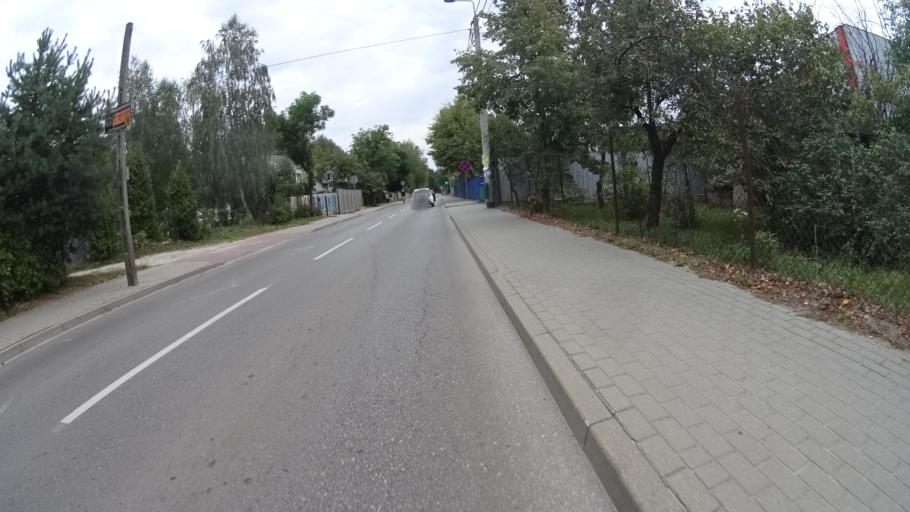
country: PL
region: Masovian Voivodeship
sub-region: Powiat pruszkowski
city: Granica
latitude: 52.1356
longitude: 20.8001
